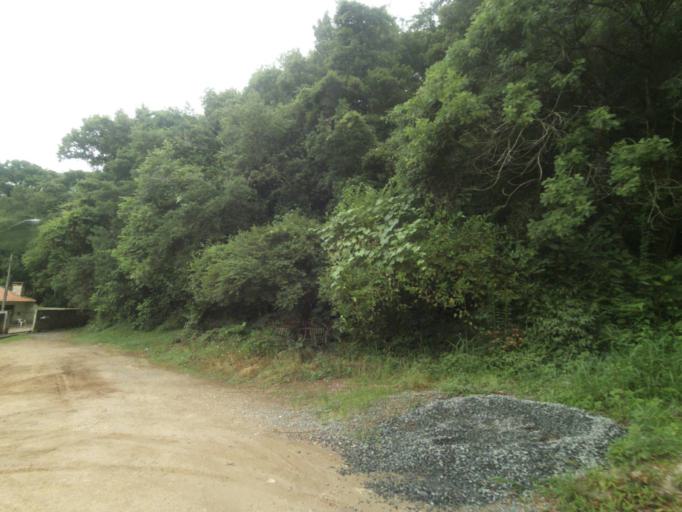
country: BR
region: Parana
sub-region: Curitiba
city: Curitiba
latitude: -25.4266
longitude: -49.3174
